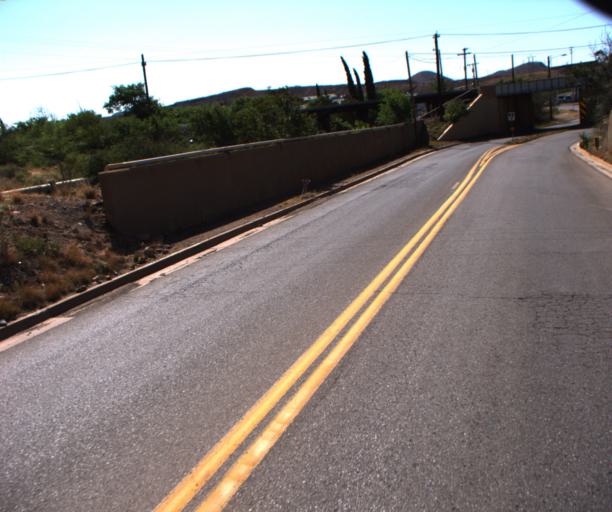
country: US
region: Arizona
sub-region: Cochise County
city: Bisbee
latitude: 31.4308
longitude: -109.8932
